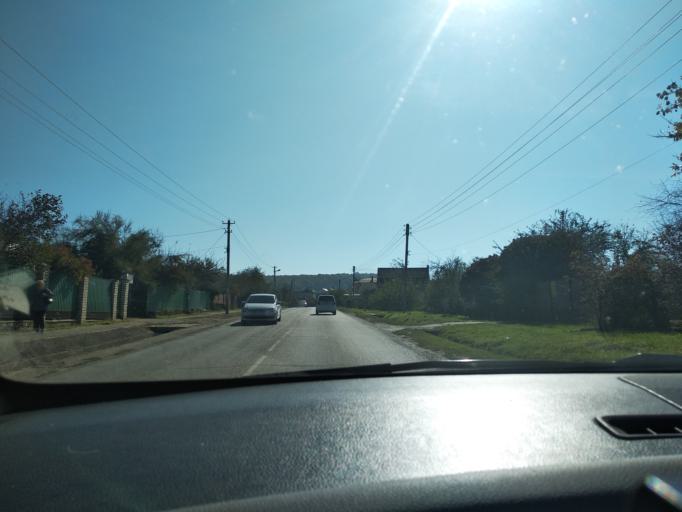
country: RU
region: Krasnodarskiy
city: Goryachiy Klyuch
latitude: 44.6321
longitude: 39.1425
